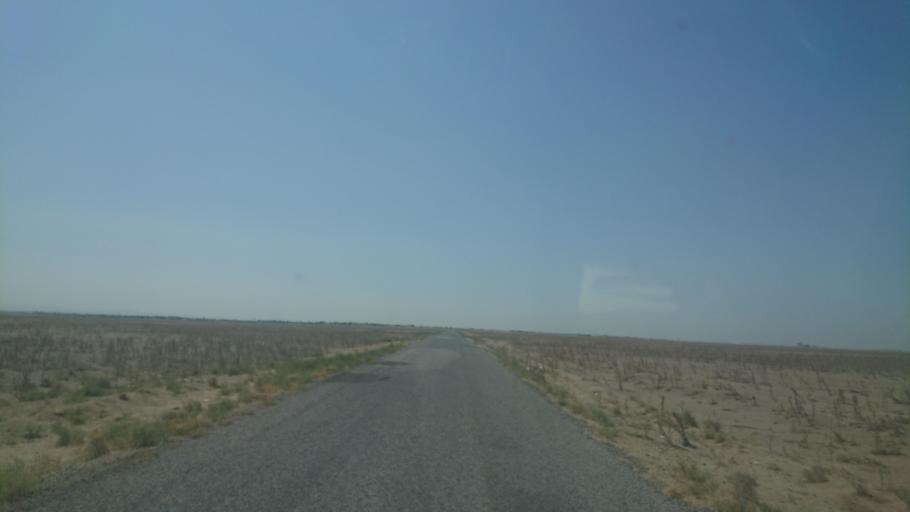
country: TR
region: Aksaray
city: Yesilova
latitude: 38.3107
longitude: 33.7373
